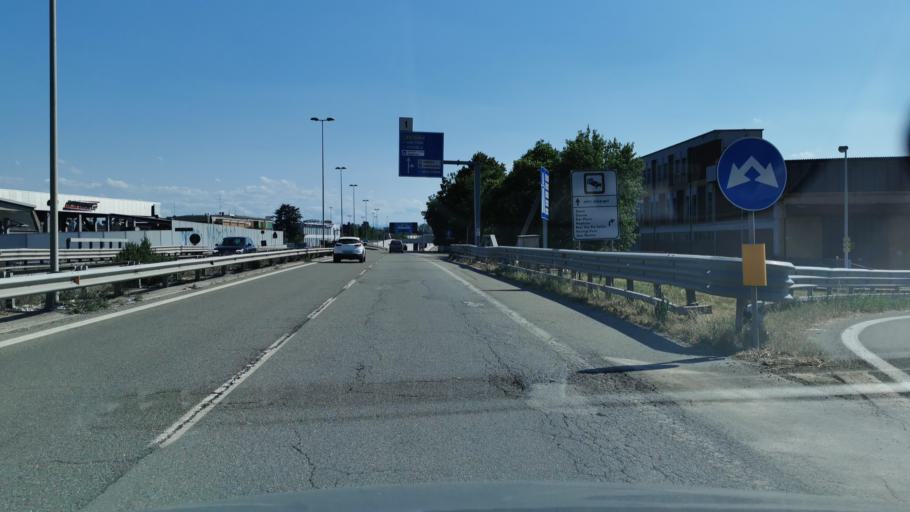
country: IT
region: Emilia-Romagna
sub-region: Provincia di Modena
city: Modena
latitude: 44.6362
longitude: 10.9585
